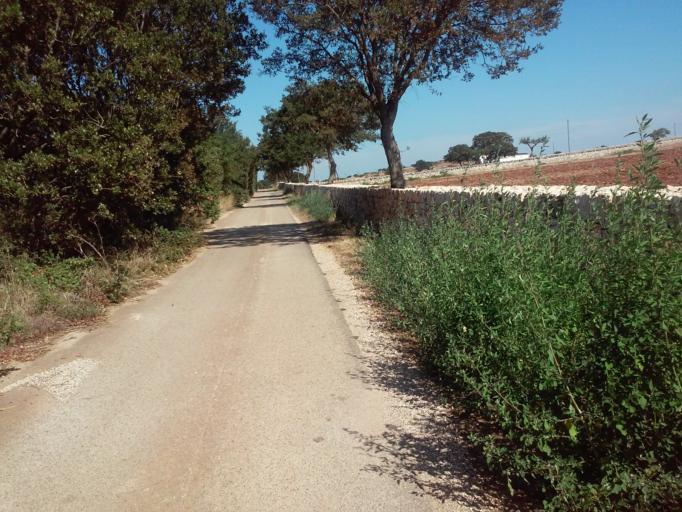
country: IT
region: Apulia
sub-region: Provincia di Bari
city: Sammichele di Bari
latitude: 40.8214
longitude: 17.0177
